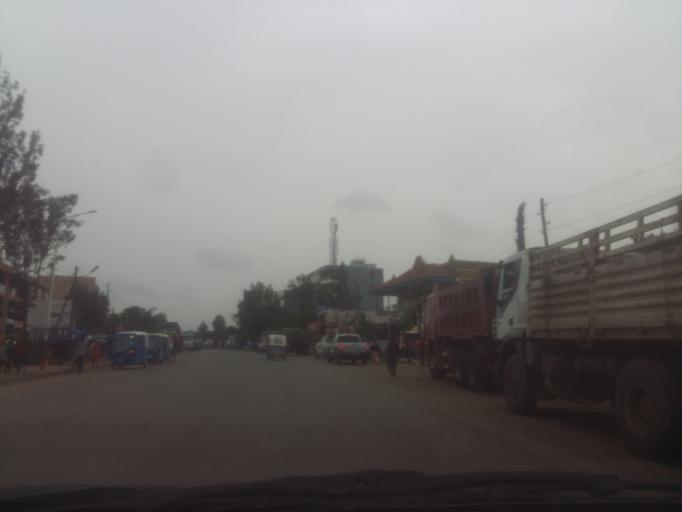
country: ET
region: Oromiya
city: Bishoftu
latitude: 8.7925
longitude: 38.9042
